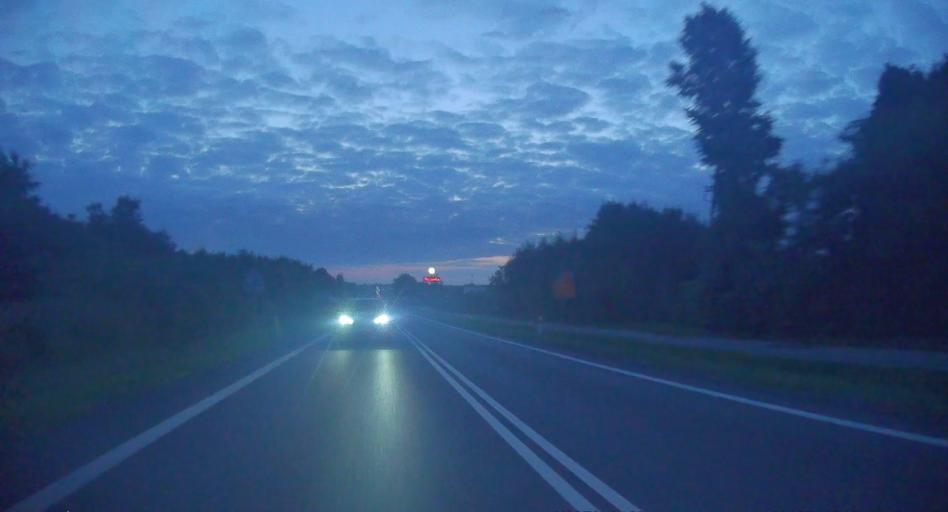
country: PL
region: Silesian Voivodeship
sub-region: Powiat klobucki
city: Klobuck
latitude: 50.8981
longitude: 18.9447
